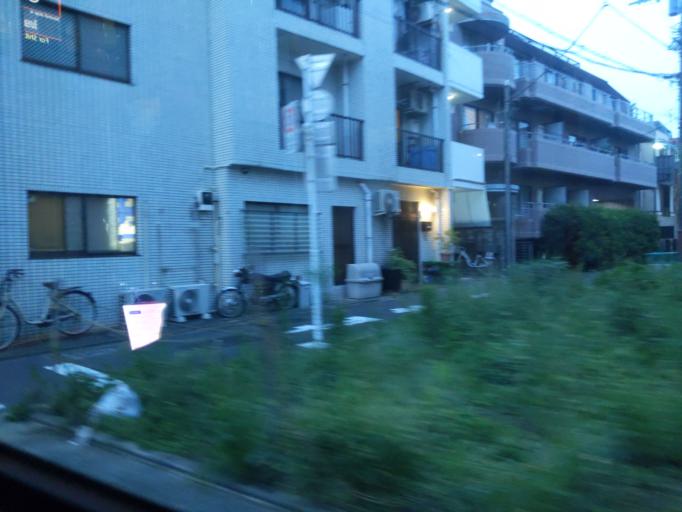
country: JP
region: Tokyo
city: Tokyo
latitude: 35.6295
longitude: 139.6950
